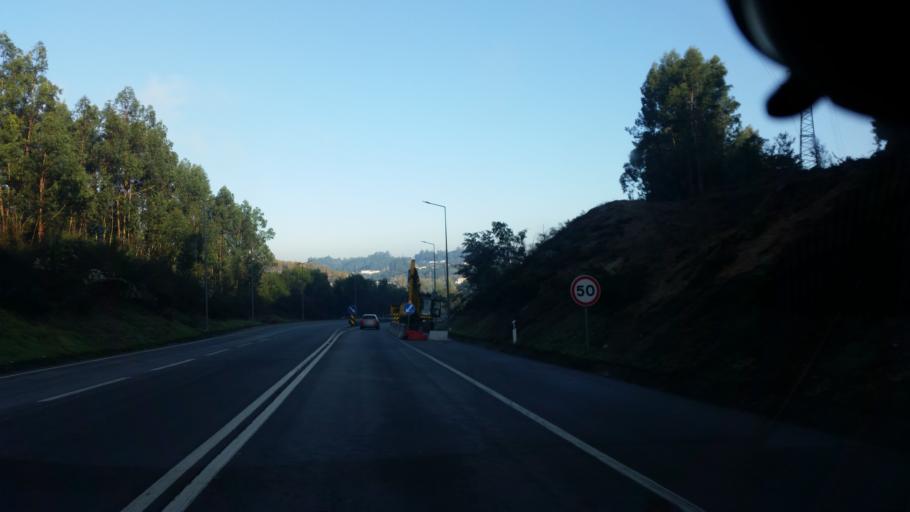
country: PT
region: Porto
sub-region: Santo Tirso
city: Sao Miguel do Couto
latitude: 41.3402
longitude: -8.4673
